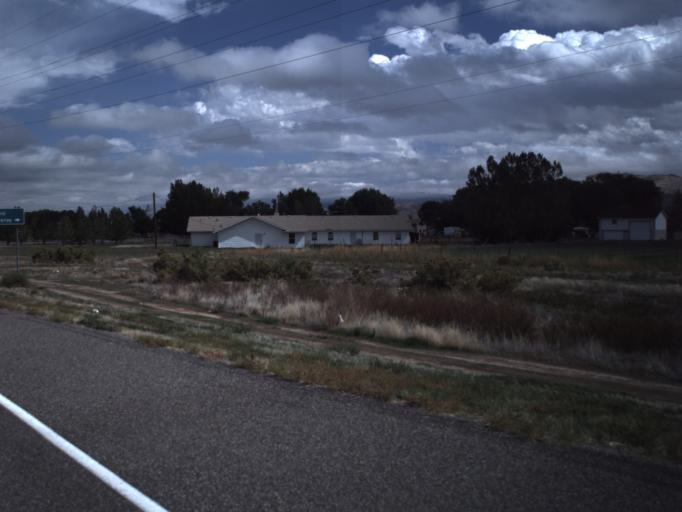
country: US
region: Utah
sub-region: Sevier County
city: Richfield
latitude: 38.7186
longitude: -112.1028
